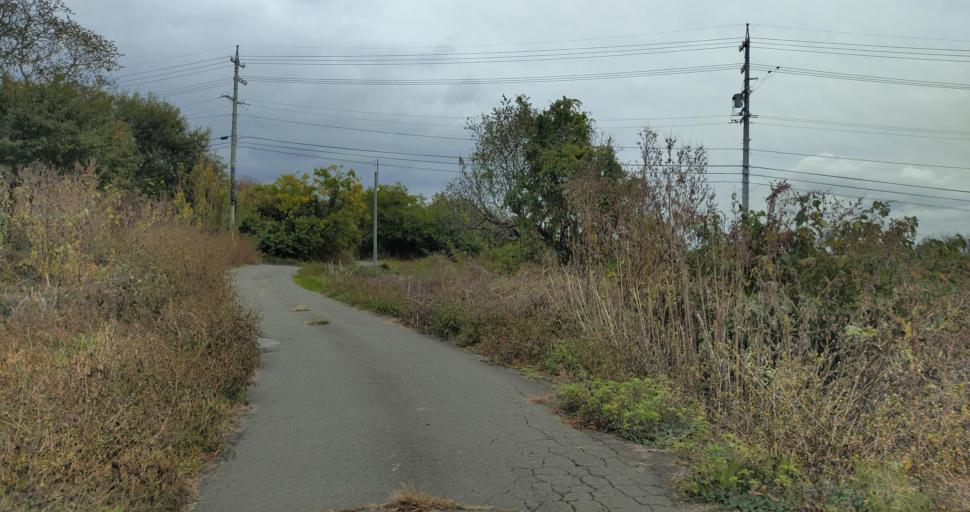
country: JP
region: Nagano
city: Komoro
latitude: 36.3611
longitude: 138.3832
